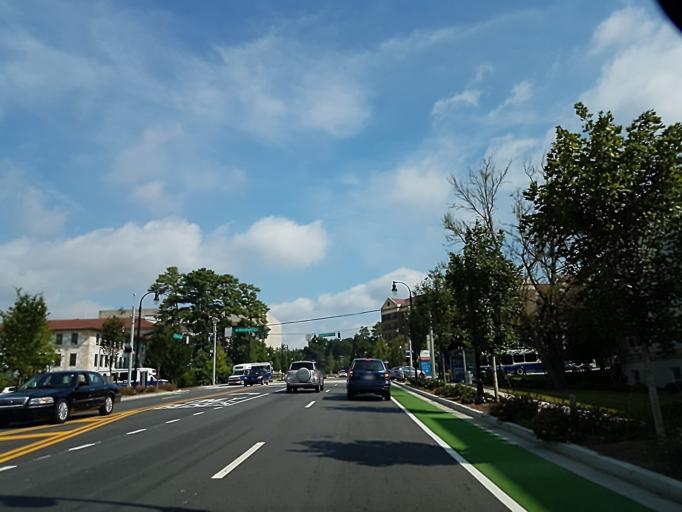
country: US
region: Georgia
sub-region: DeKalb County
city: North Decatur
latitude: 33.7925
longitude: -84.3209
